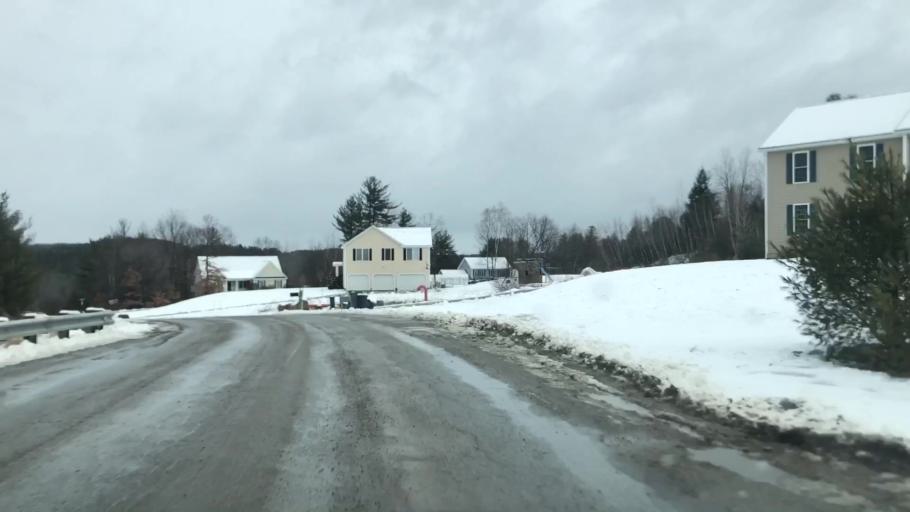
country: US
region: New Hampshire
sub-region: Hillsborough County
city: New Boston
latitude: 42.9952
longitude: -71.6603
